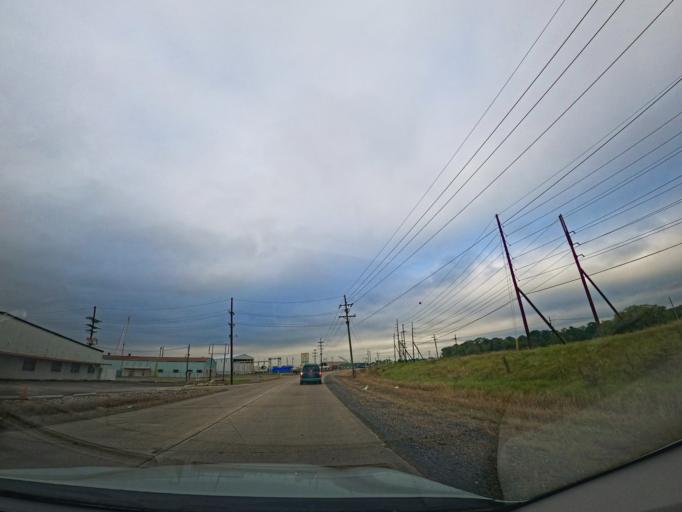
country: US
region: Louisiana
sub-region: Terrebonne Parish
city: Houma
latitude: 29.5736
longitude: -90.7054
